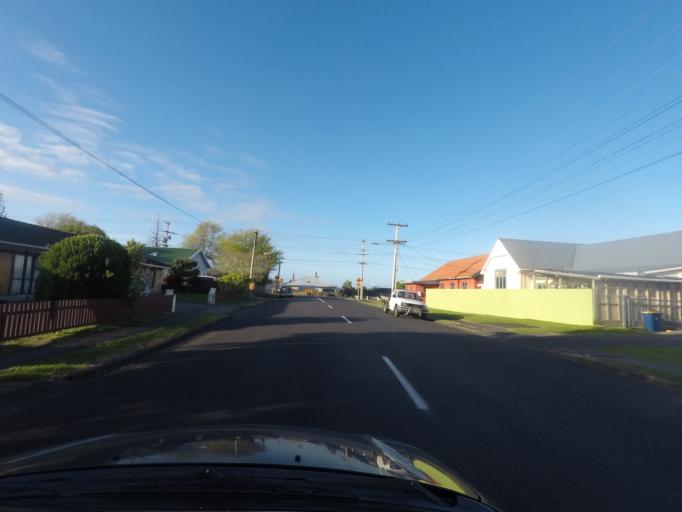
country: NZ
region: Auckland
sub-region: Auckland
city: Waitakere
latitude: -36.9060
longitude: 174.6740
